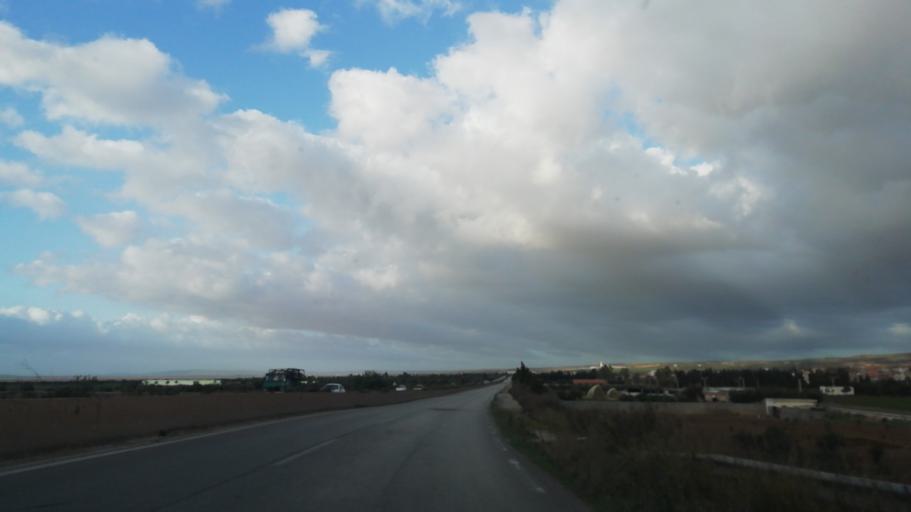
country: DZ
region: Oran
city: Bou Tlelis
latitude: 35.5680
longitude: -0.8866
